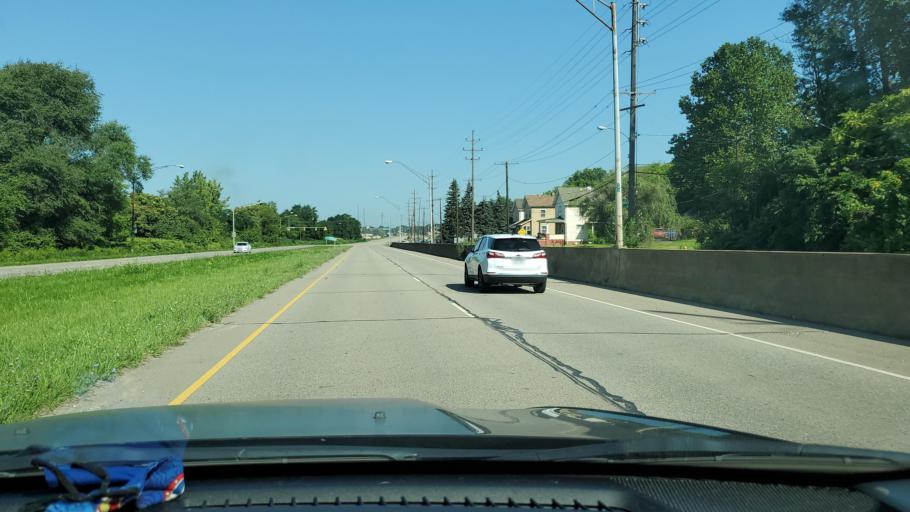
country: US
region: Ohio
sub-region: Trumbull County
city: Girard
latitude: 41.1281
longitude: -80.6814
